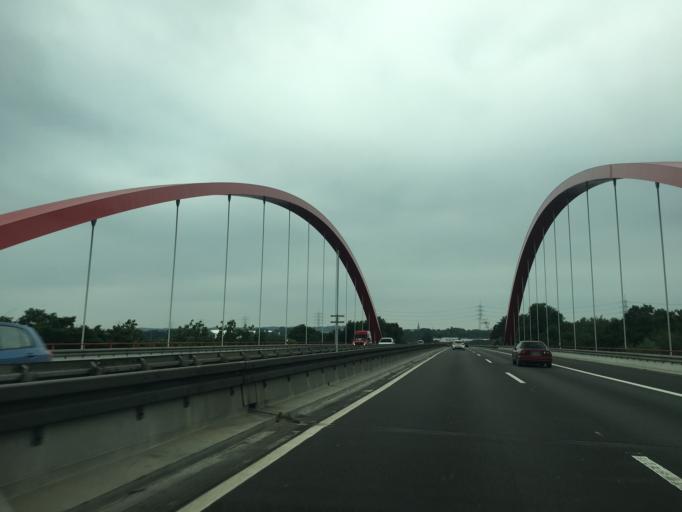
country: DE
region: North Rhine-Westphalia
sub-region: Regierungsbezirk Munster
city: Bottrop
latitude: 51.5051
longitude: 6.9764
